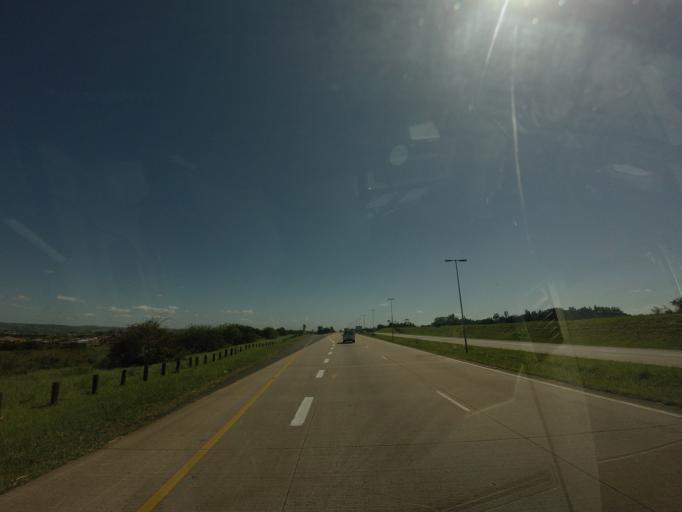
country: ZA
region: KwaZulu-Natal
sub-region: iLembe District Municipality
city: Stanger
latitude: -29.4108
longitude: 31.2804
